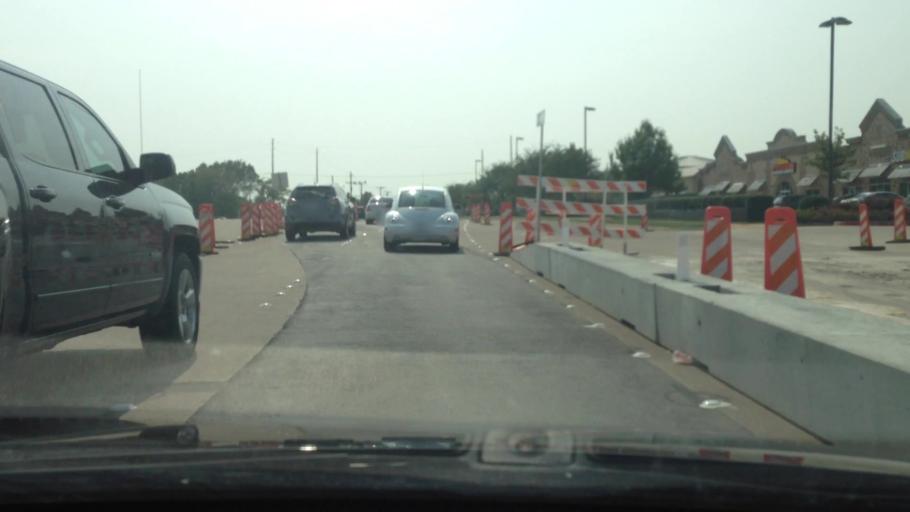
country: US
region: Texas
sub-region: Tarrant County
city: North Richland Hills
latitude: 32.8621
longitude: -97.2100
